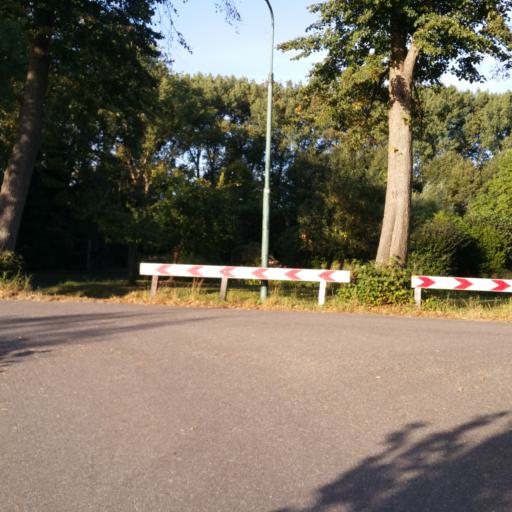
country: NL
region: Utrecht
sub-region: Gemeente Lopik
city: Lopik
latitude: 51.9702
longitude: 4.9774
